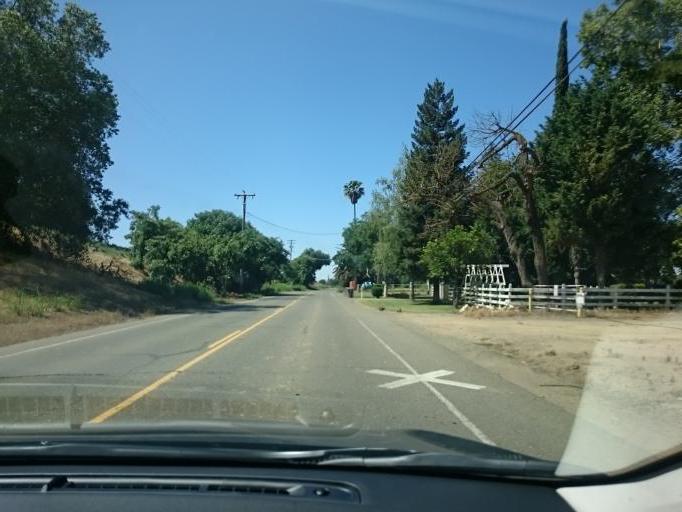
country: US
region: California
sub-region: Yolo County
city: West Sacramento
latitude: 38.5148
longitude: -121.5540
